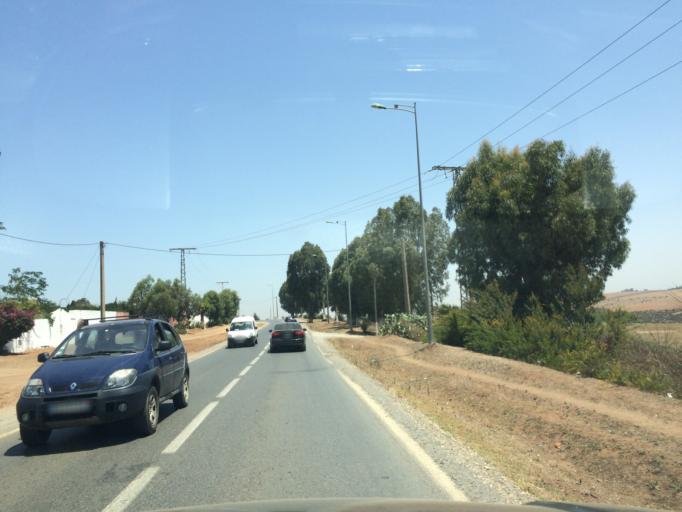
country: MA
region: Rabat-Sale-Zemmour-Zaer
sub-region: Skhirate-Temara
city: Temara
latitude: 33.8770
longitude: -6.8467
